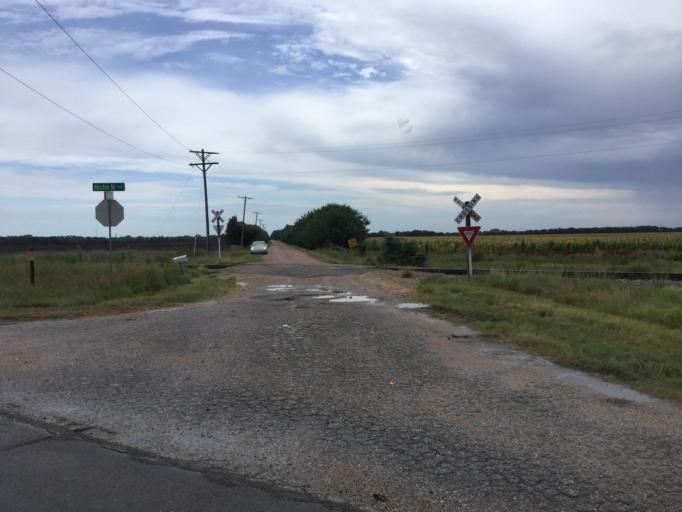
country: US
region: Kansas
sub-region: Harvey County
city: Hesston
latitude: 38.1629
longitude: -97.4637
